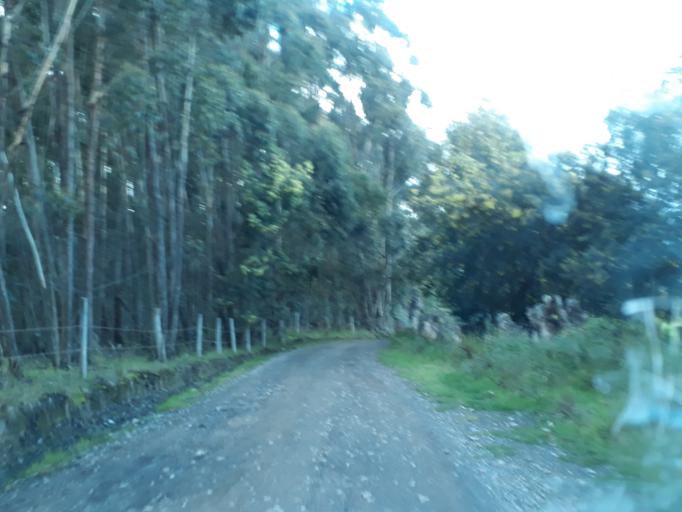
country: CO
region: Cundinamarca
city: Carmen de Carupa
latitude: 5.3339
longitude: -73.9092
